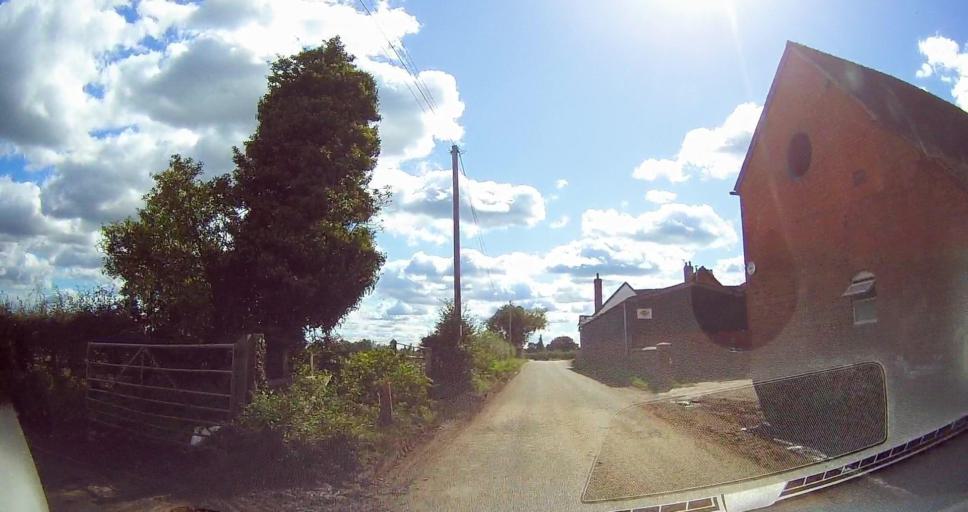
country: GB
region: England
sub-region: Cheshire East
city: Nantwich
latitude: 52.9889
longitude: -2.5338
